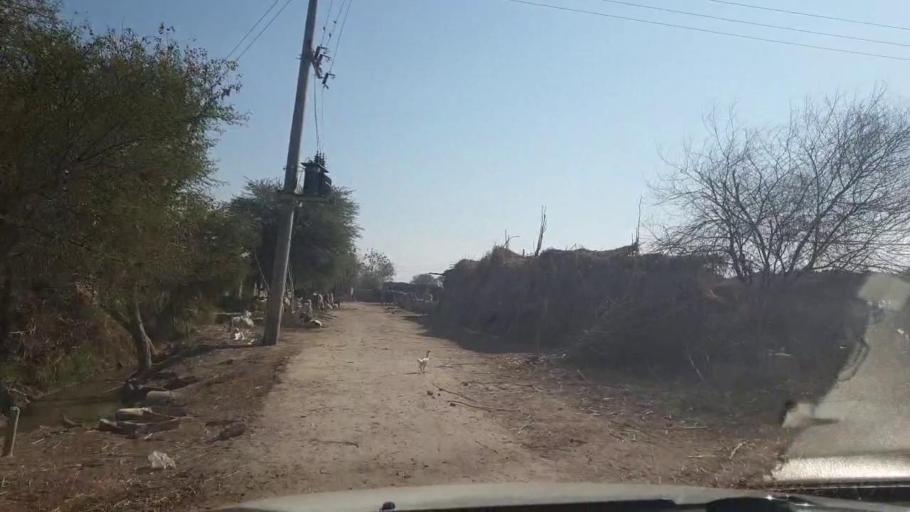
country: PK
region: Sindh
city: Mirpur Khas
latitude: 25.5106
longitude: 69.1374
